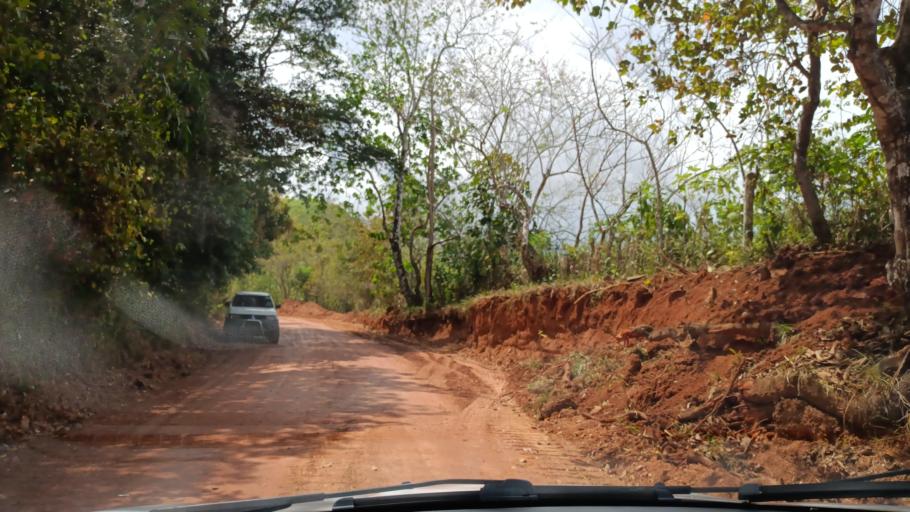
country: PA
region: Panama
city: La Cabima
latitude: 9.1197
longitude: -79.4959
